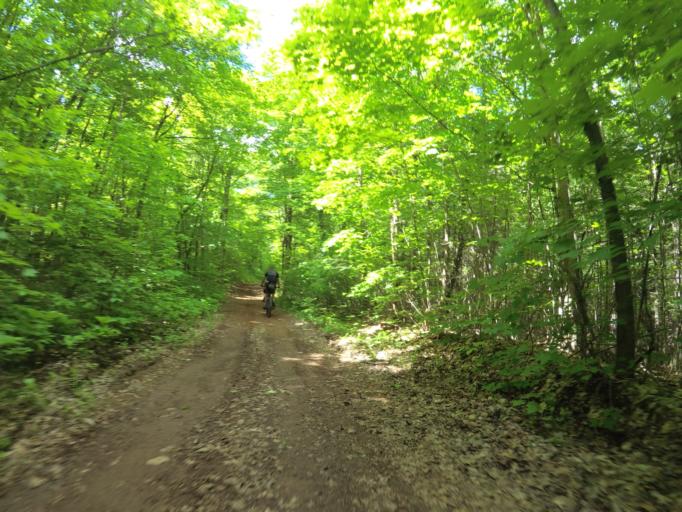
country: CA
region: Ontario
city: Renfrew
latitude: 45.0708
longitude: -76.7969
